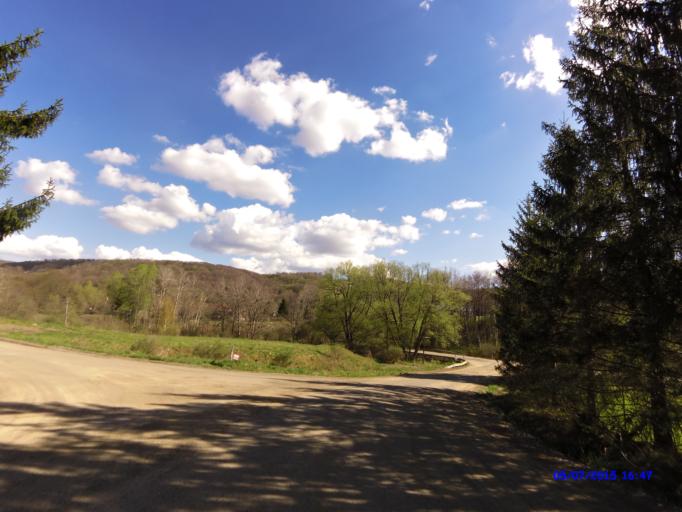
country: US
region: New York
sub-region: Cattaraugus County
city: Little Valley
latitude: 42.2768
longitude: -78.6978
